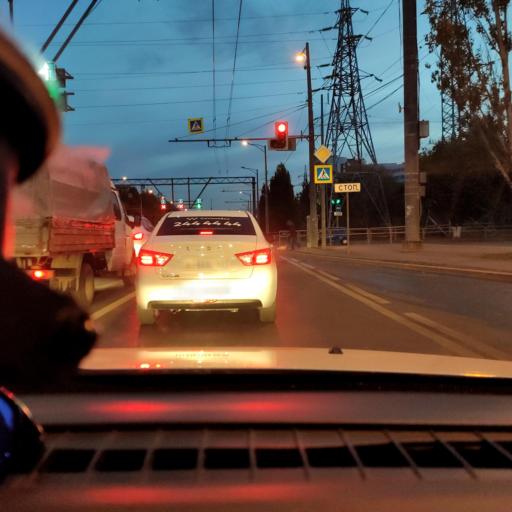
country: RU
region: Samara
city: Samara
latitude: 53.2403
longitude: 50.2061
